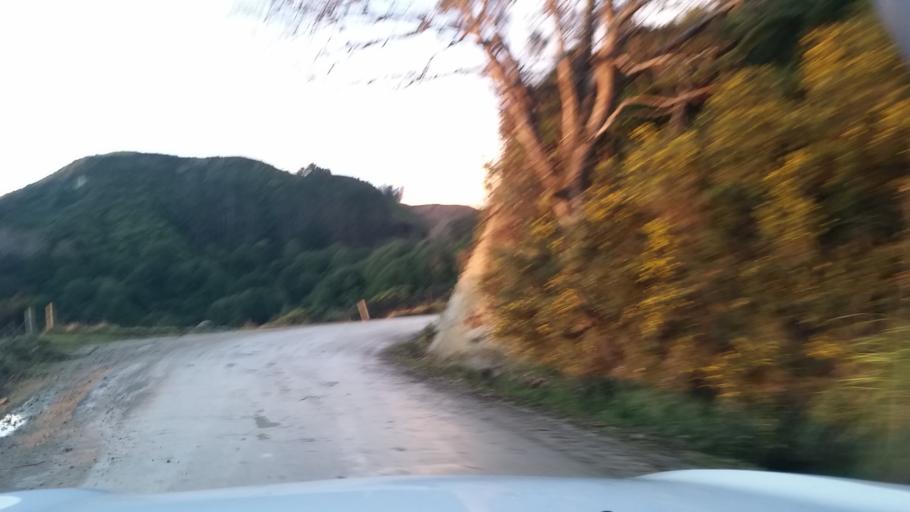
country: NZ
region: Manawatu-Wanganui
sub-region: Wanganui District
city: Wanganui
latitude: -39.7590
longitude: 174.8835
